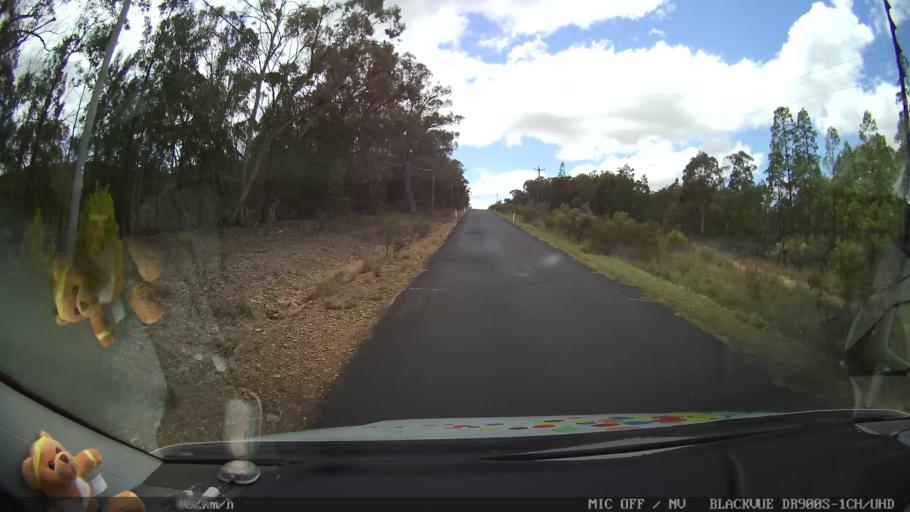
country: AU
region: New South Wales
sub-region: Glen Innes Severn
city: Glen Innes
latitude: -29.4409
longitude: 151.6165
